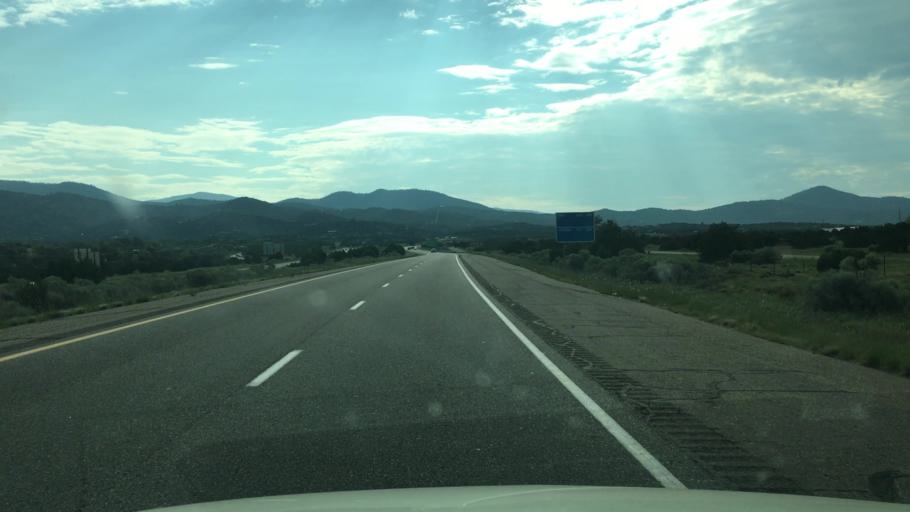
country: US
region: New Mexico
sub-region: Santa Fe County
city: Santa Fe
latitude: 35.6370
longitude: -105.9463
